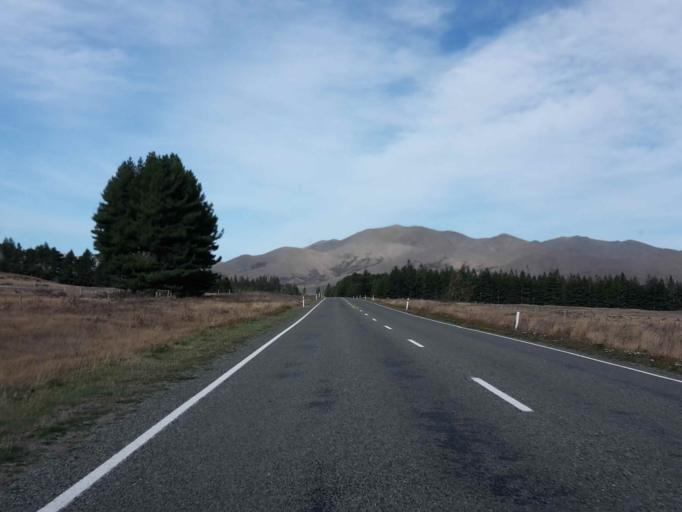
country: NZ
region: Canterbury
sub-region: Timaru District
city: Pleasant Point
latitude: -44.0810
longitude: 170.5332
